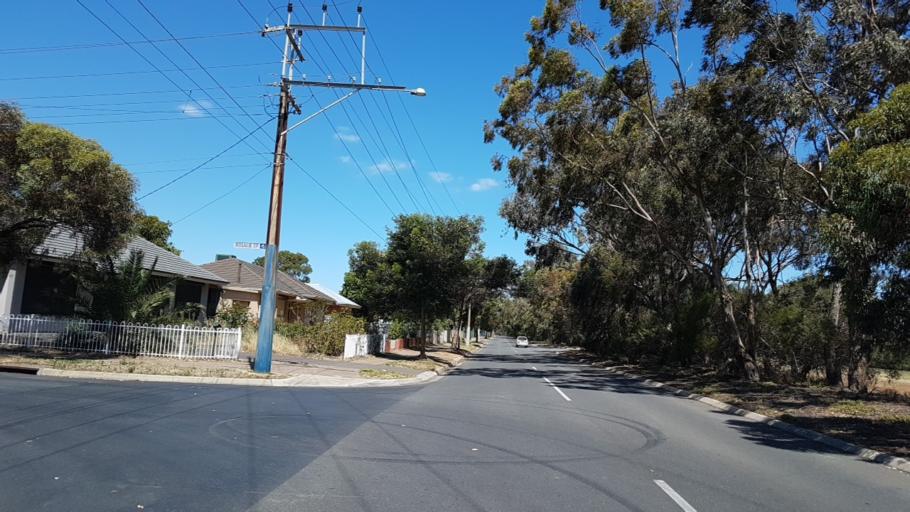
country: AU
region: South Australia
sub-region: Salisbury
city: Salisbury
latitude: -34.7933
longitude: 138.6062
